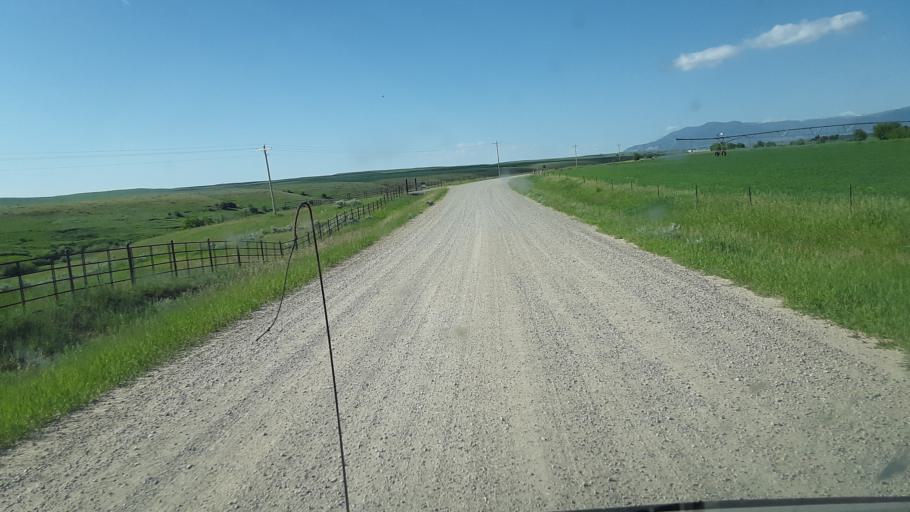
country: US
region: Montana
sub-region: Carbon County
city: Red Lodge
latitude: 45.3482
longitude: -109.1559
